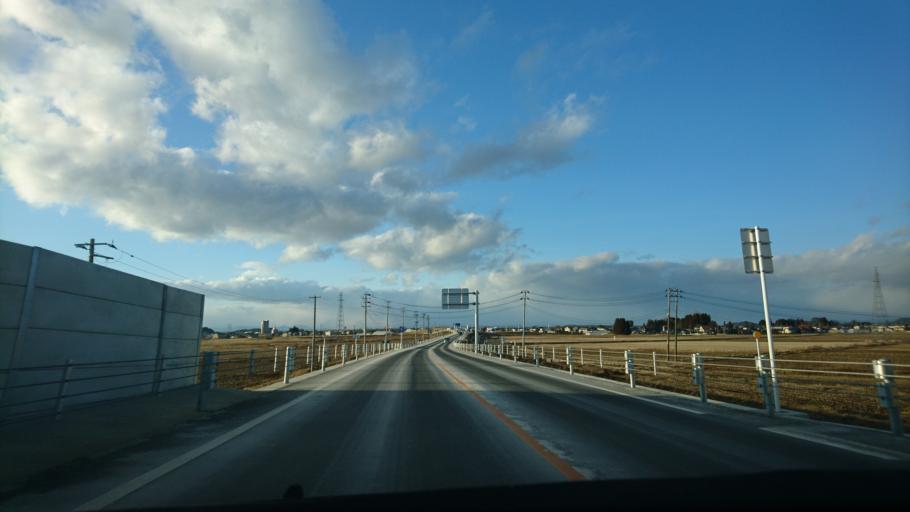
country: JP
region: Miyagi
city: Wakuya
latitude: 38.6898
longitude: 141.2204
